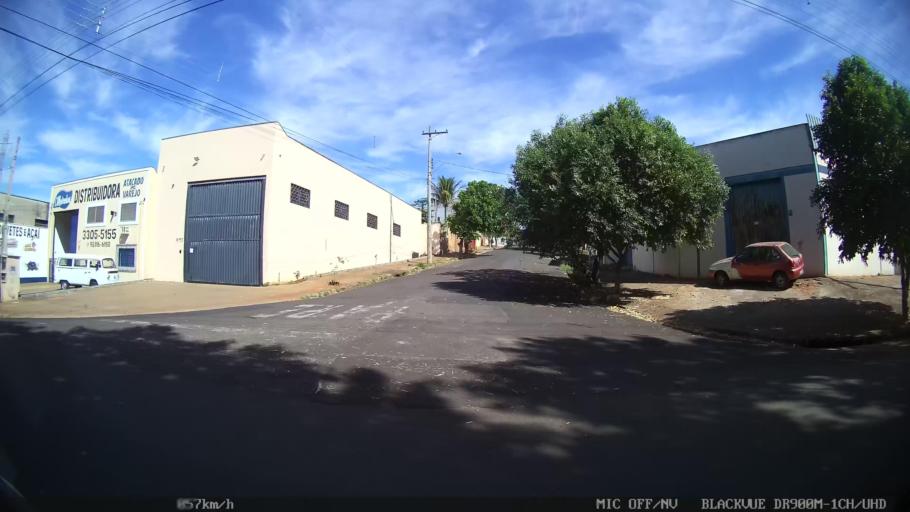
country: BR
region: Sao Paulo
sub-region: Sao Jose Do Rio Preto
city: Sao Jose do Rio Preto
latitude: -20.8418
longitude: -49.3637
